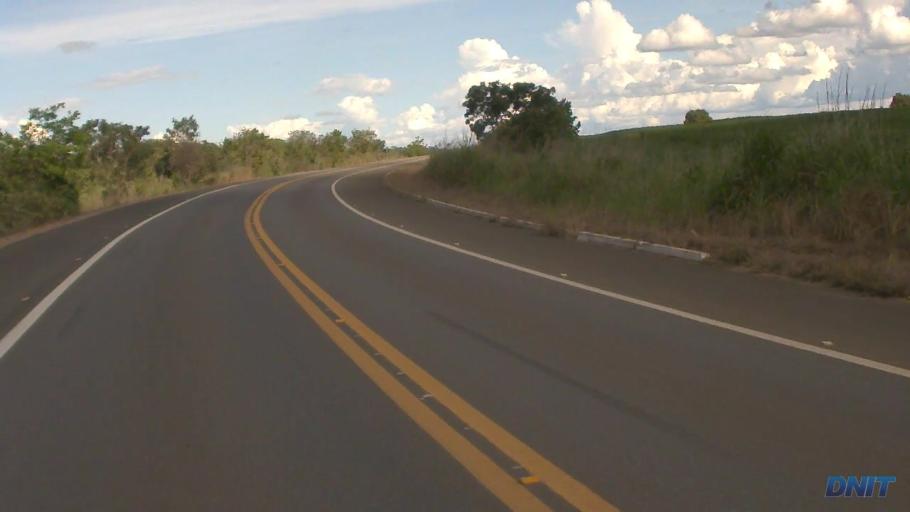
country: BR
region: Goias
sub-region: Padre Bernardo
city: Padre Bernardo
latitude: -15.2121
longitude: -48.5631
